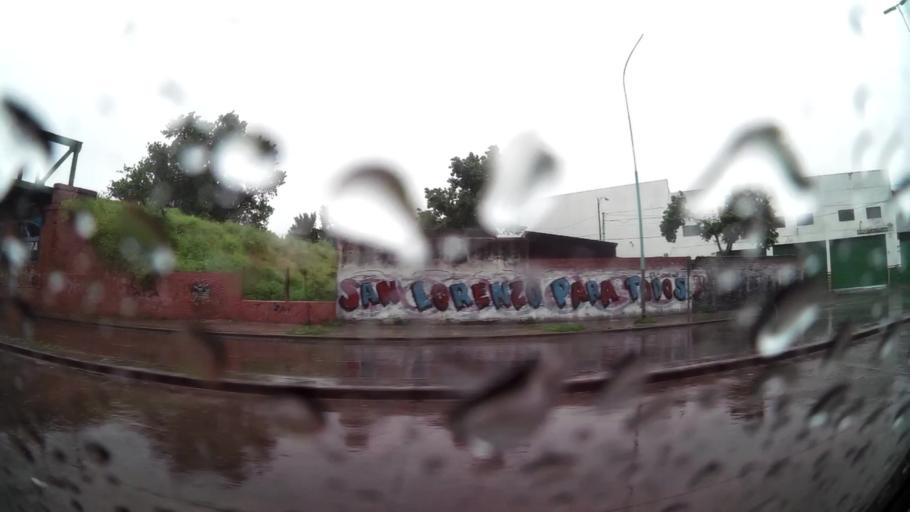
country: AR
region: Buenos Aires F.D.
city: Villa Lugano
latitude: -34.6504
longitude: -58.4295
